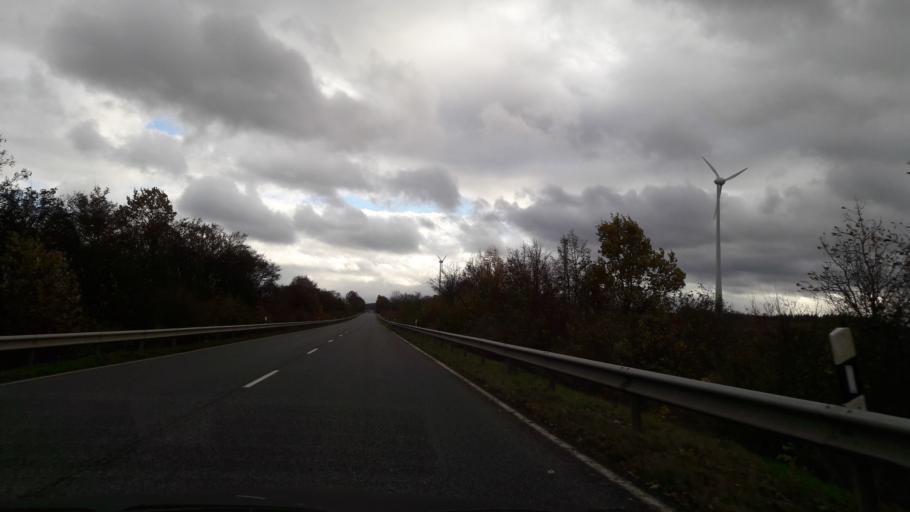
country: DE
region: Rheinland-Pfalz
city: Fell
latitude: 49.7521
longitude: 6.7760
